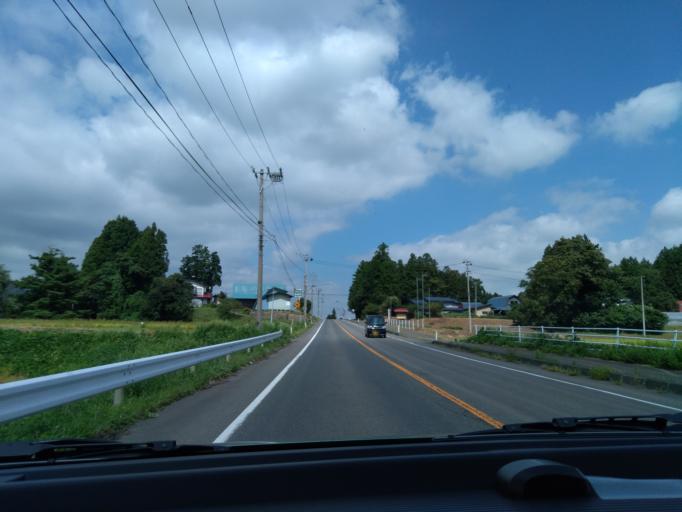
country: JP
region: Iwate
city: Hanamaki
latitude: 39.4217
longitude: 141.0759
